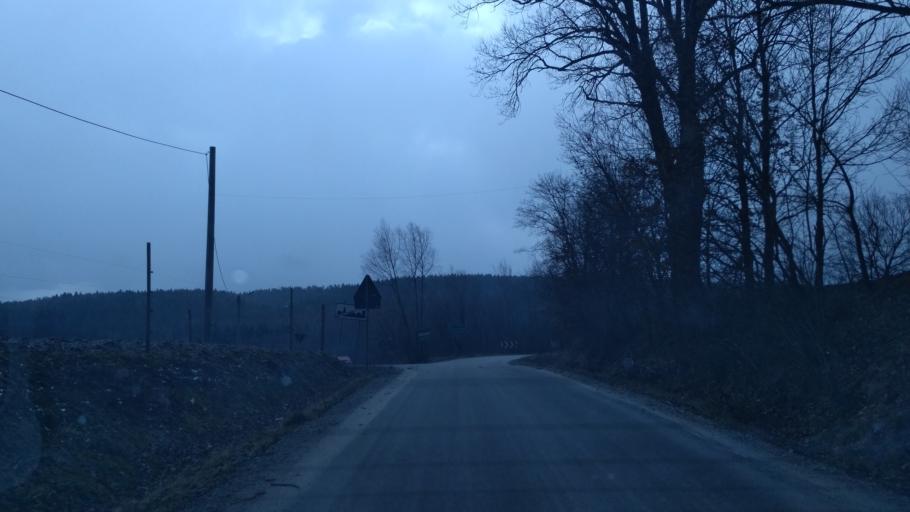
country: PL
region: Subcarpathian Voivodeship
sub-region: Powiat rzeszowski
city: Hyzne
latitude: 49.9027
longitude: 22.1961
